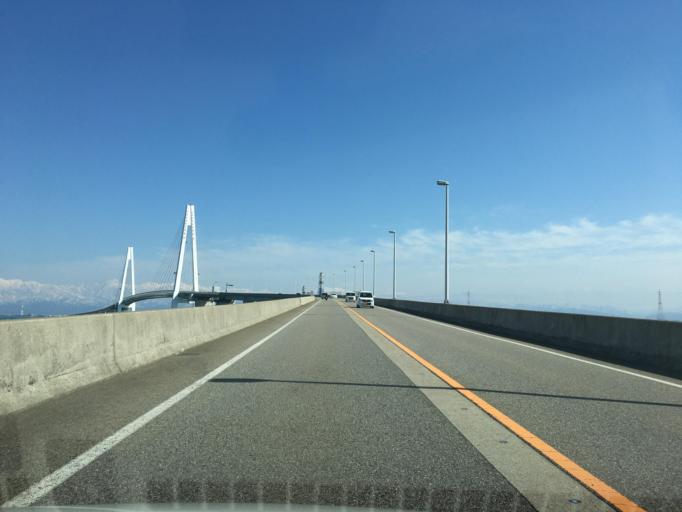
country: JP
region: Toyama
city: Nishishinminato
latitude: 36.7786
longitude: 137.1090
